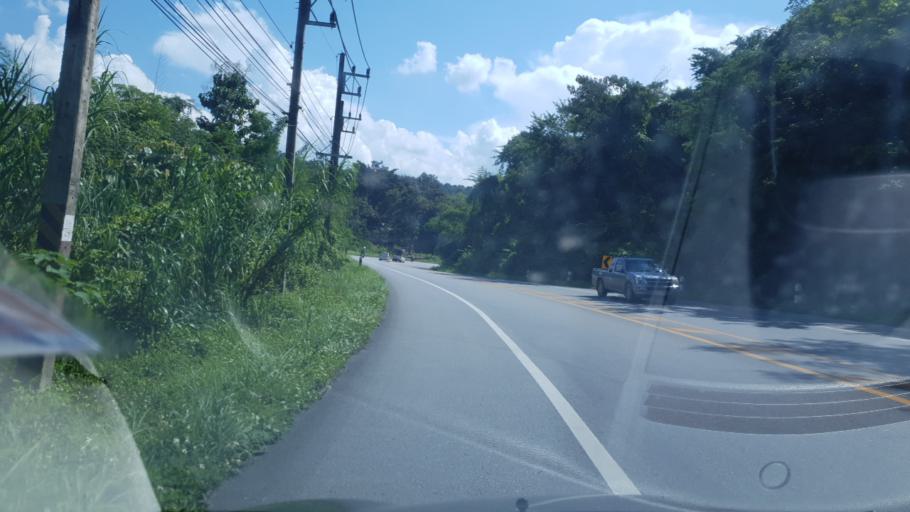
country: TH
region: Chiang Rai
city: Mae Suai
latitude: 19.6920
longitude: 99.5713
